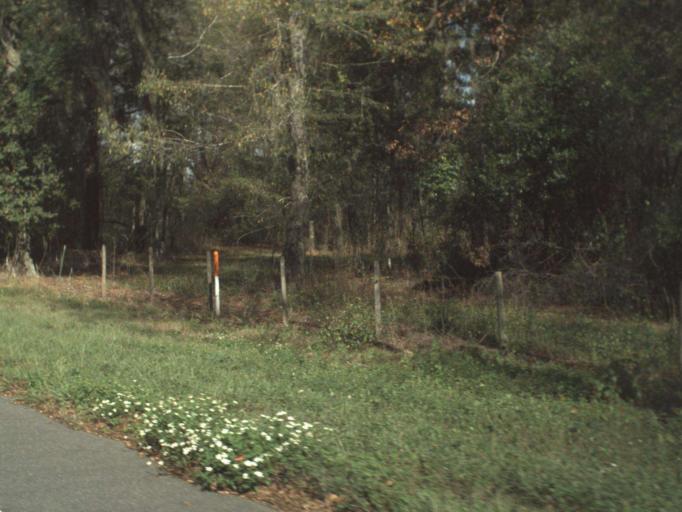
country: US
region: Florida
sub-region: Gadsden County
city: Gretna
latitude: 30.6828
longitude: -84.7137
